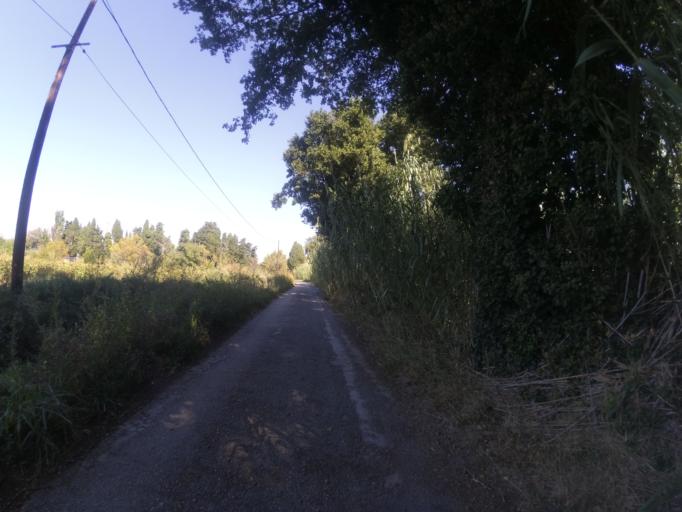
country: FR
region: Languedoc-Roussillon
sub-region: Departement des Pyrenees-Orientales
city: Pezilla-la-Riviere
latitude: 42.6881
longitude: 2.7678
